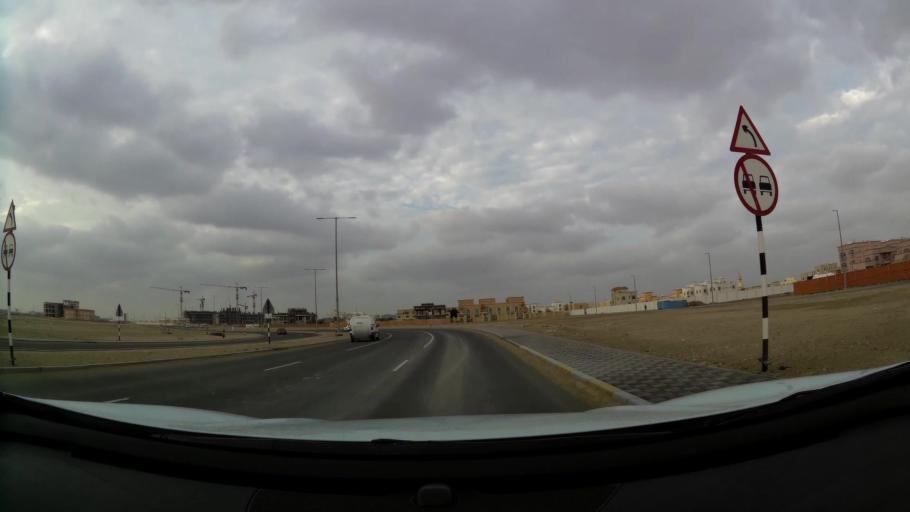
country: AE
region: Abu Dhabi
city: Abu Dhabi
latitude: 24.3492
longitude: 54.5425
